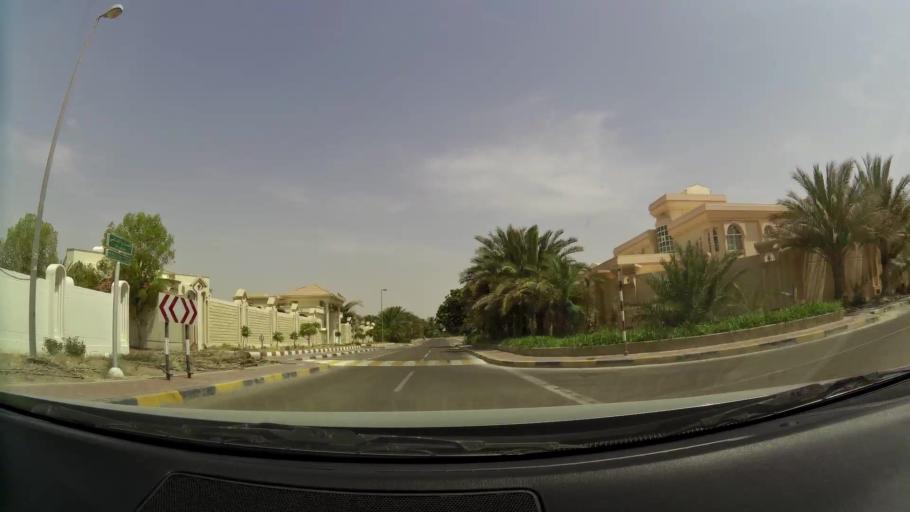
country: AE
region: Abu Dhabi
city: Al Ain
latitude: 24.1777
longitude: 55.7196
